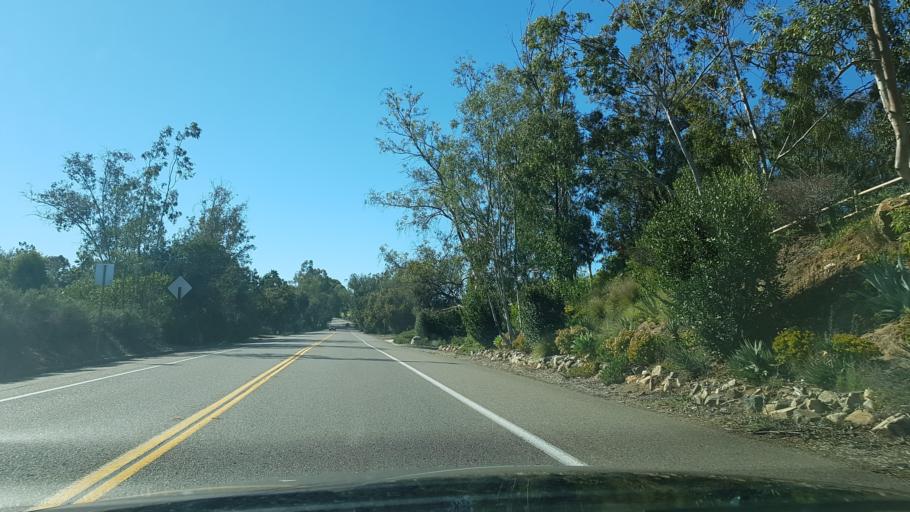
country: US
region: California
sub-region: San Diego County
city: Rancho Santa Fe
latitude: 33.0351
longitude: -117.1852
